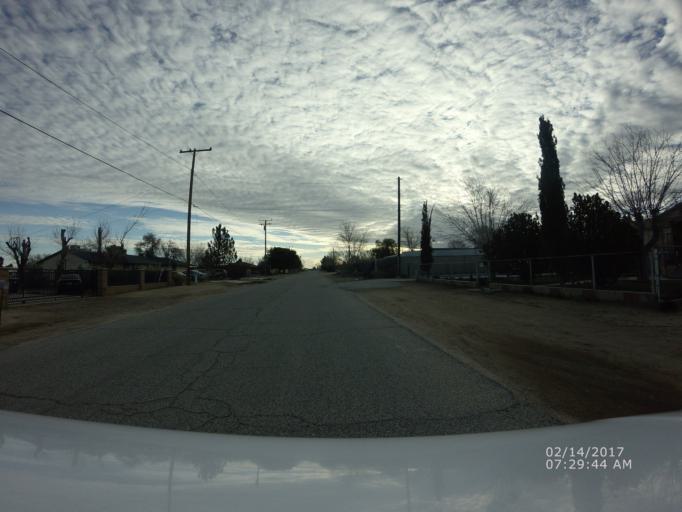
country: US
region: California
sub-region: Los Angeles County
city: Littlerock
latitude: 34.5447
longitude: -117.9442
